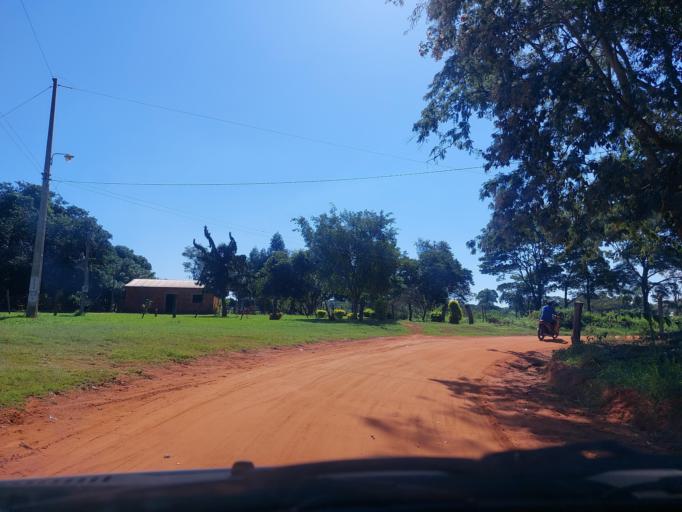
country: PY
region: San Pedro
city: Lima
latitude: -24.1624
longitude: -56.0134
